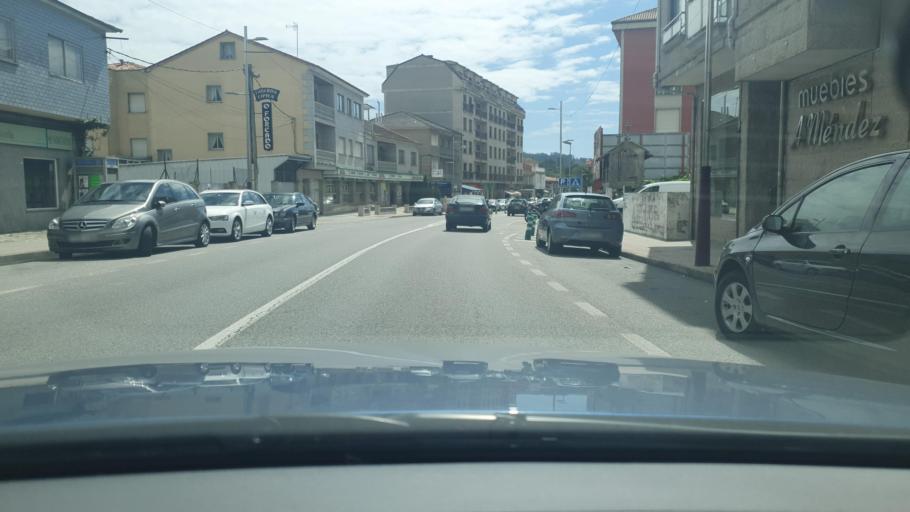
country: ES
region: Galicia
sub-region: Provincia de Pontevedra
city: Meano
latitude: 42.4500
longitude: -8.8132
